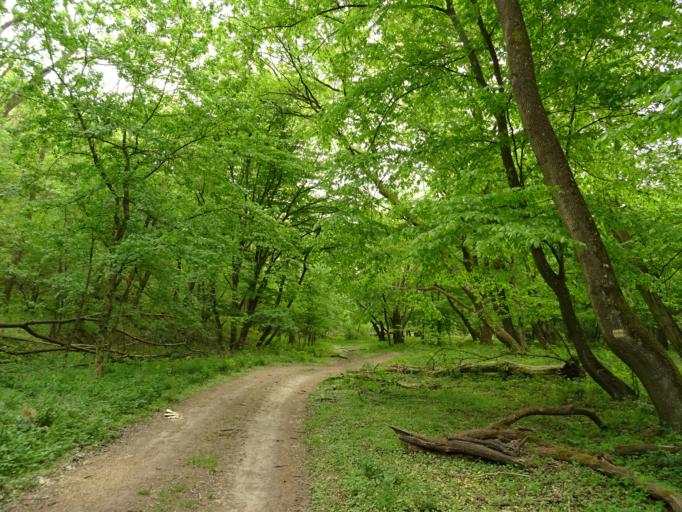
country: HU
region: Fejer
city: Szarliget
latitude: 47.4562
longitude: 18.4727
